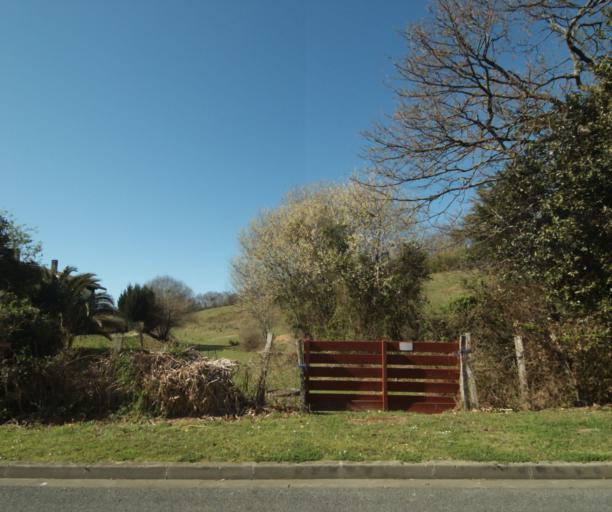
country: FR
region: Aquitaine
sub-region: Departement des Pyrenees-Atlantiques
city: Ciboure
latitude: 43.3896
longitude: -1.6890
